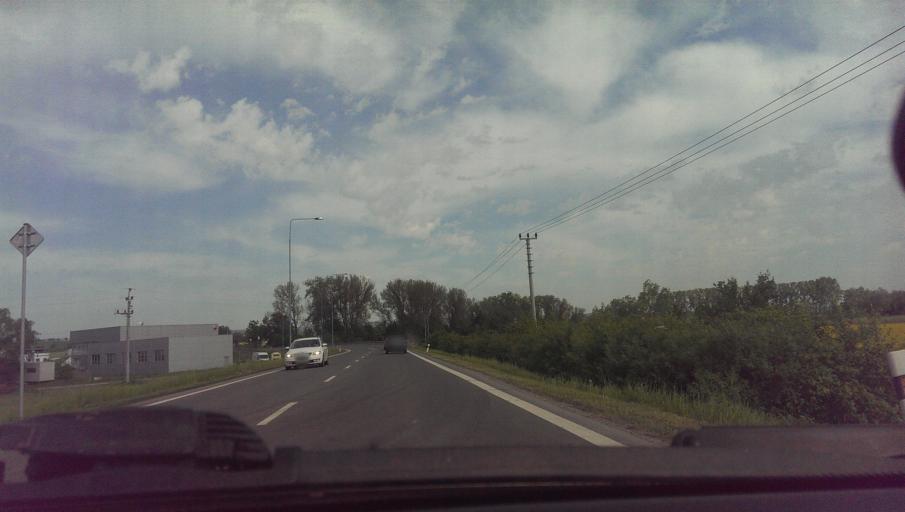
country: CZ
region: Zlin
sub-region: Okres Uherske Hradiste
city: Uherske Hradiste
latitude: 49.0846
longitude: 17.4511
